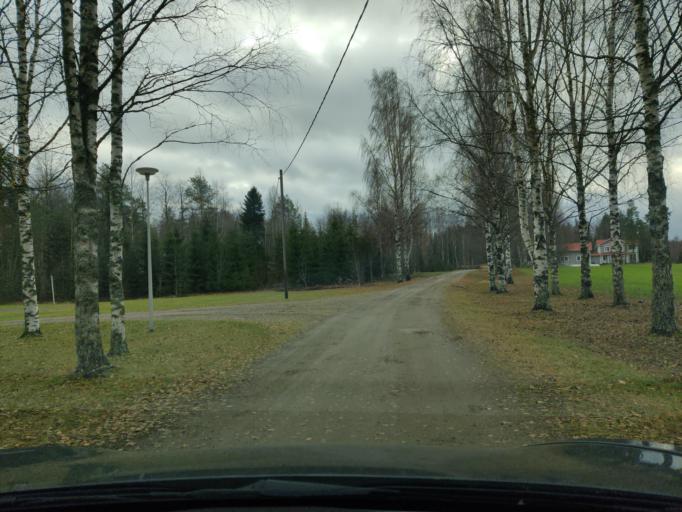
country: FI
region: Northern Savo
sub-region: Ylae-Savo
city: Kiuruvesi
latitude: 63.6417
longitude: 26.6541
